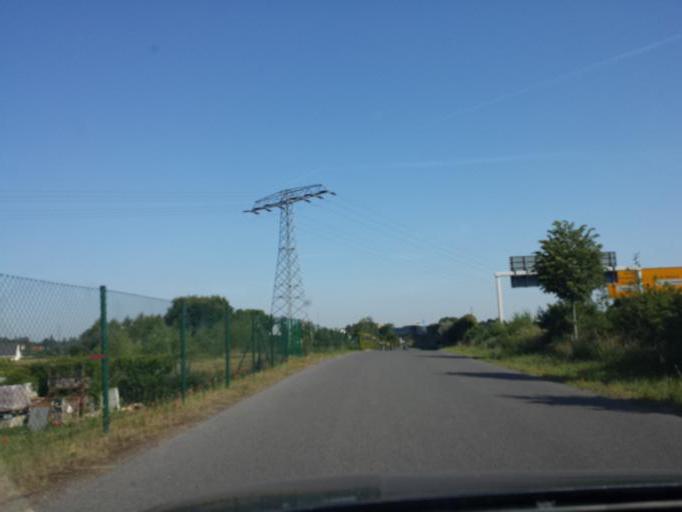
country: DE
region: Berlin
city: Lichtenrade
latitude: 52.3511
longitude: 13.4350
